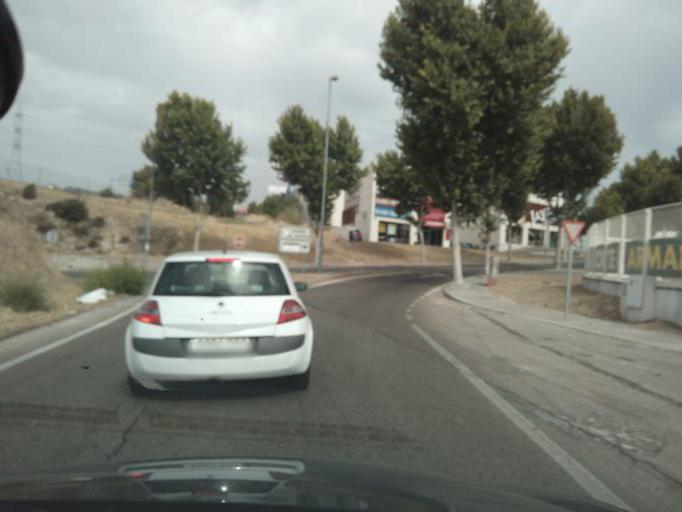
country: ES
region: Madrid
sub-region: Provincia de Madrid
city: Las Rozas de Madrid
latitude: 40.4969
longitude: -3.8892
